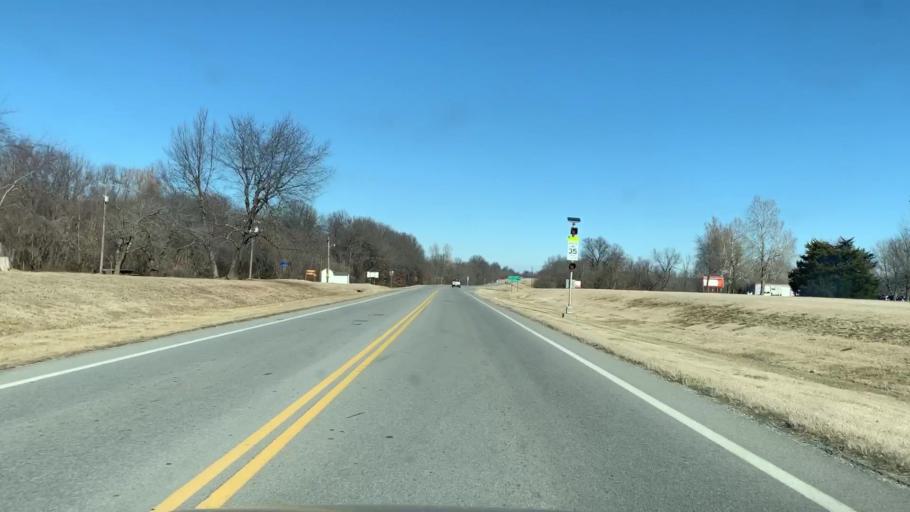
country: US
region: Kansas
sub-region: Cherokee County
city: Baxter Springs
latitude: 37.0360
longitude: -94.7348
